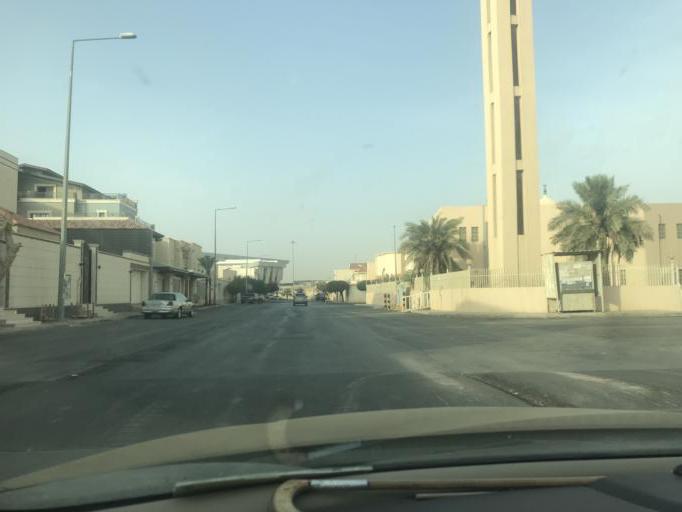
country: SA
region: Ar Riyad
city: Riyadh
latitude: 24.7429
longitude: 46.7505
